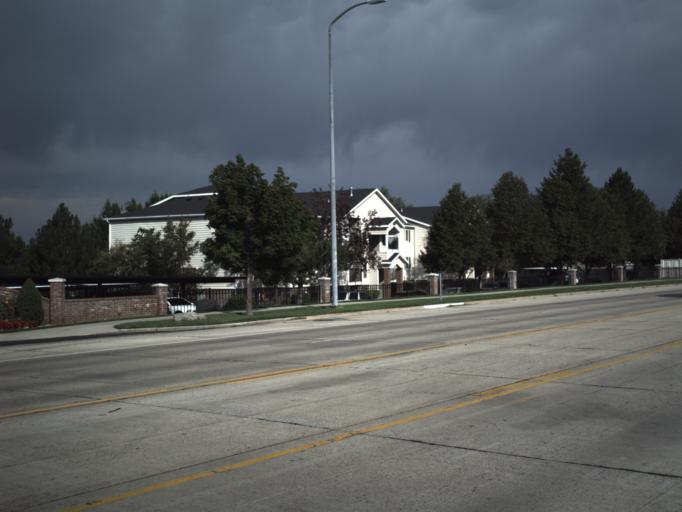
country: US
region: Utah
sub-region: Weber County
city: Harrisville
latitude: 41.2656
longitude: -111.9694
